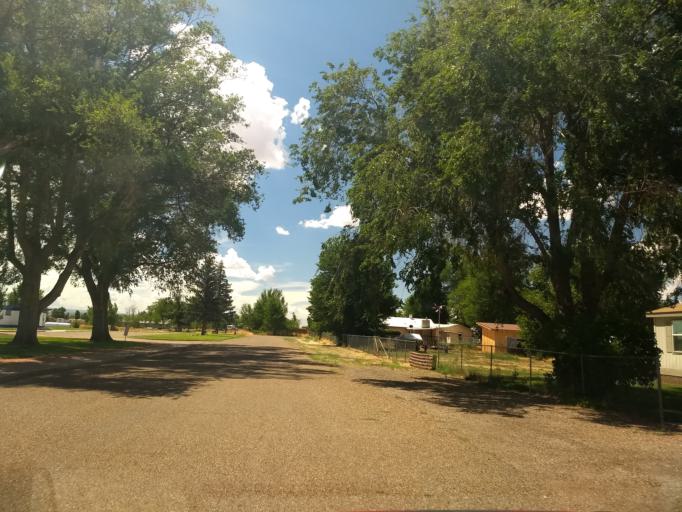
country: US
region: Arizona
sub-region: Coconino County
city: Fredonia
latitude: 36.9501
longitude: -112.5221
